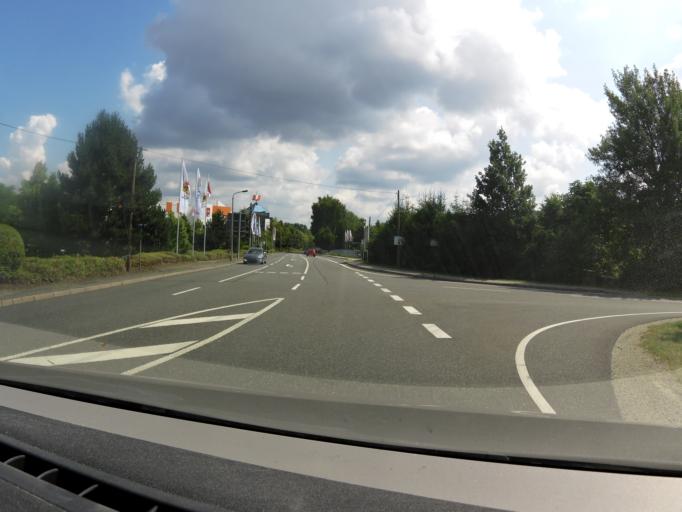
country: DE
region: Thuringia
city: Martinroda
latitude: 50.6971
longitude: 10.8981
